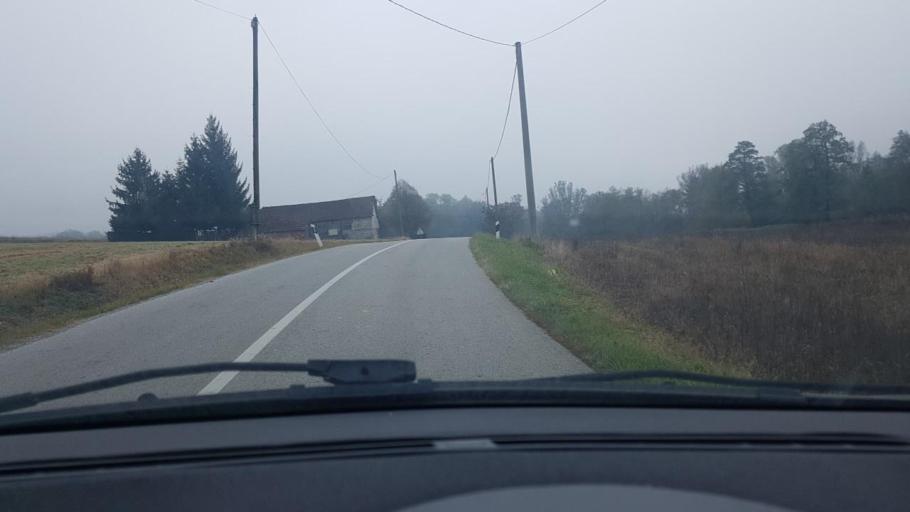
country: HR
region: Varazdinska
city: Ivanec
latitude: 46.1356
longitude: 16.1780
